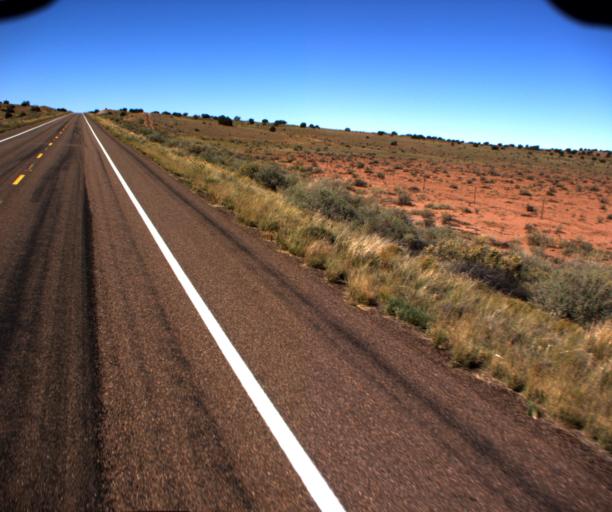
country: US
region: Arizona
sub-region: Apache County
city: Saint Johns
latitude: 34.5932
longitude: -109.6136
